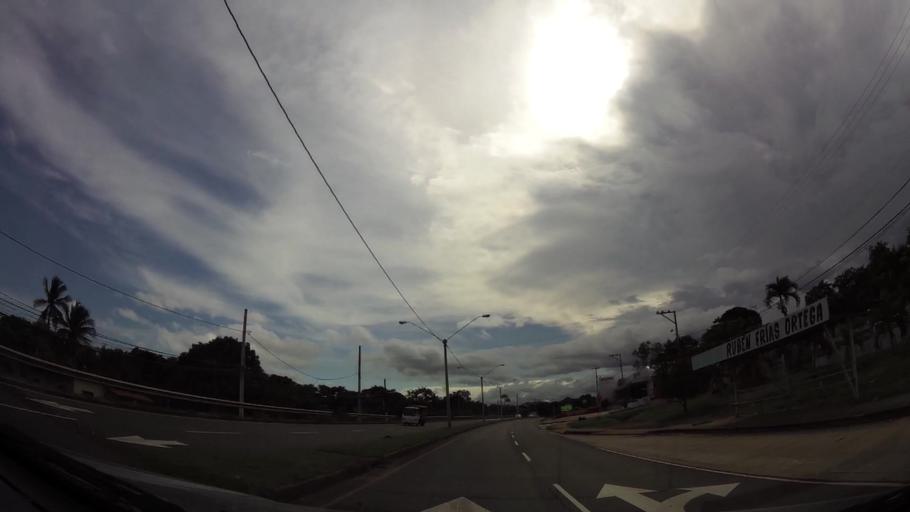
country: PA
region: Panama
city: El Coco
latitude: 8.8653
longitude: -79.8033
